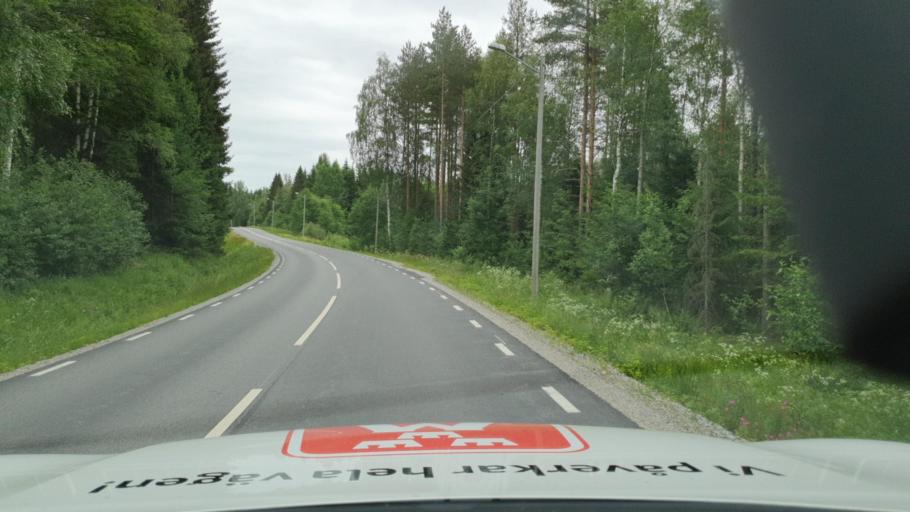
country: SE
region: Vaesterbotten
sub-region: Nordmalings Kommun
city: Nordmaling
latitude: 63.5295
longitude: 19.3652
